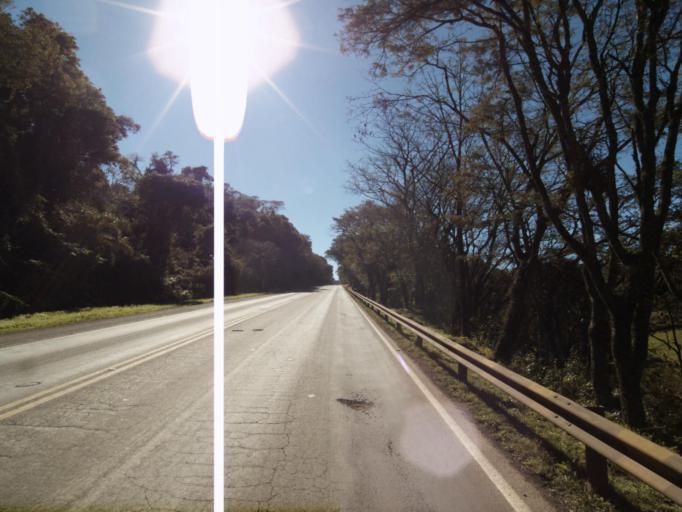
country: BR
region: Rio Grande do Sul
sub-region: Frederico Westphalen
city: Frederico Westphalen
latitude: -26.8021
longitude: -53.3109
